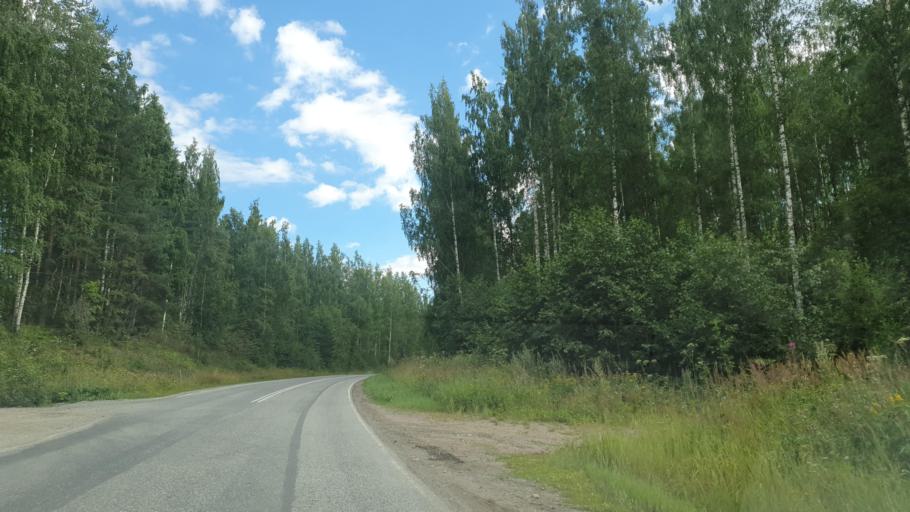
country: FI
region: Central Finland
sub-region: Jyvaeskylae
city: Muurame
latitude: 62.1454
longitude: 25.7159
